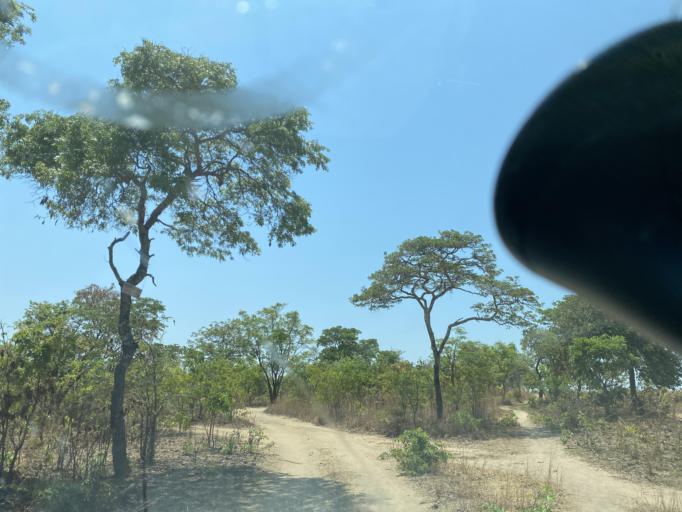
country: ZM
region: Lusaka
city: Chongwe
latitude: -15.4297
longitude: 29.1882
